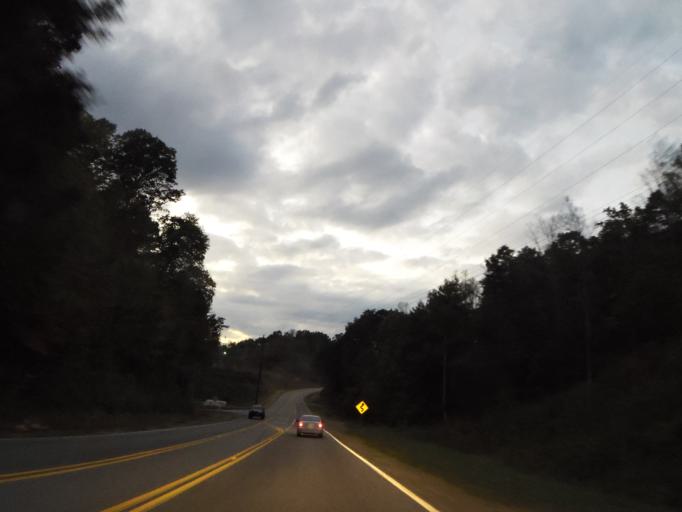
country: US
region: North Carolina
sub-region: Madison County
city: Marshall
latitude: 35.8481
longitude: -82.7313
